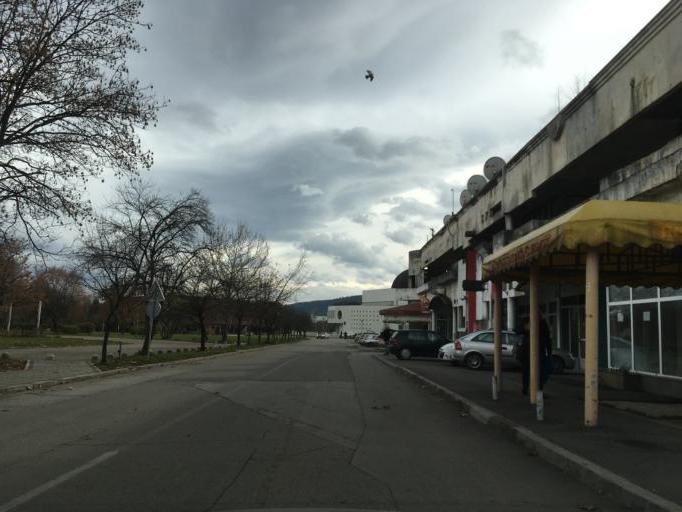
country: BA
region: Federation of Bosnia and Herzegovina
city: Bugojno
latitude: 44.0533
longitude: 17.4442
